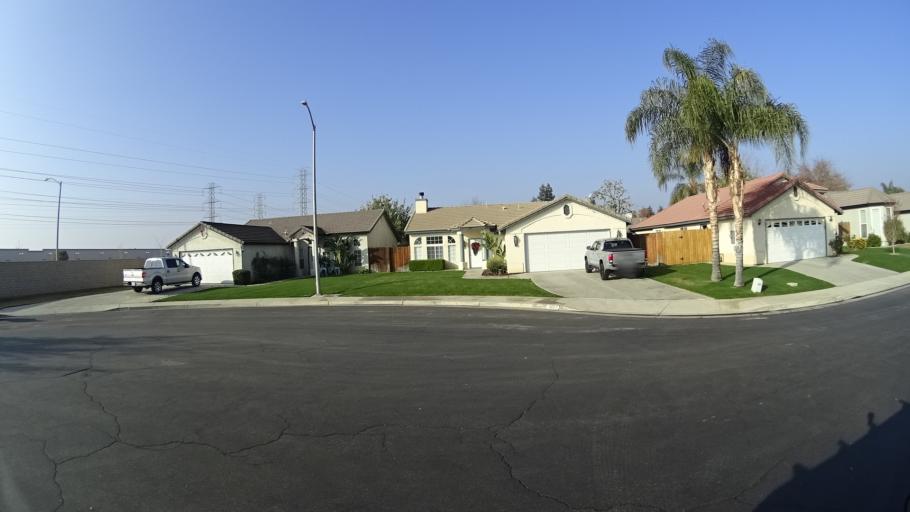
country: US
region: California
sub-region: Kern County
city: Greenacres
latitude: 35.3872
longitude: -119.0984
